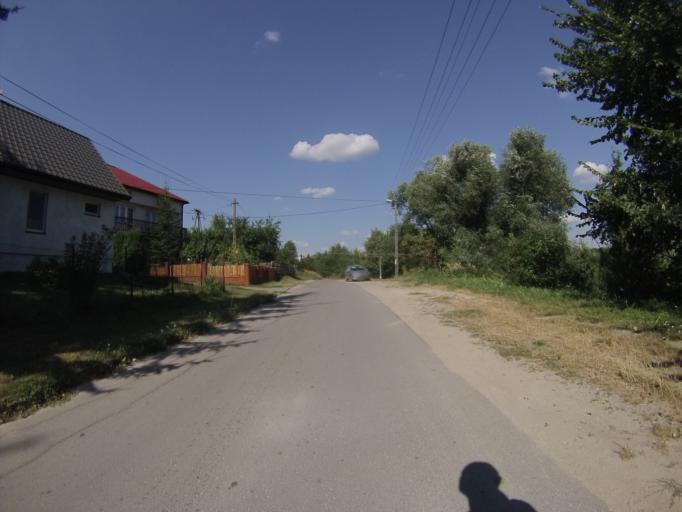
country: PL
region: Swietokrzyskie
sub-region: Powiat kielecki
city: Rakow
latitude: 50.6724
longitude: 21.0393
